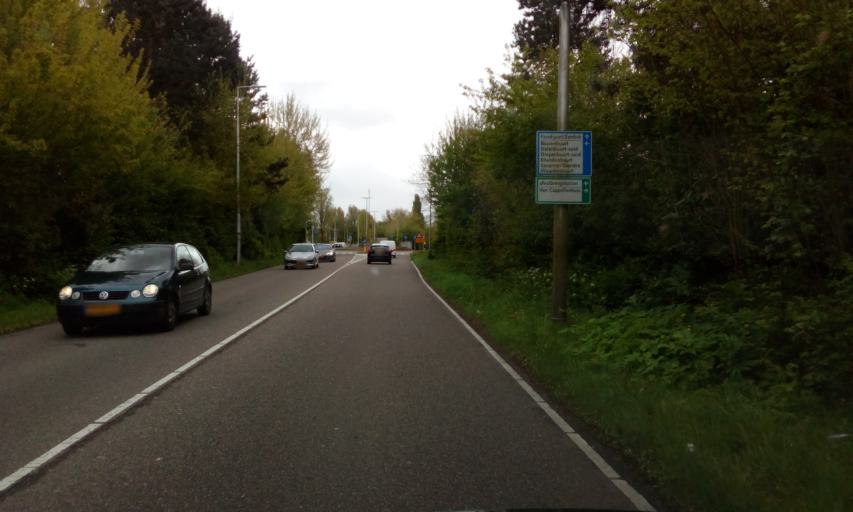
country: NL
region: South Holland
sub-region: Gemeente Krimpen aan den IJssel
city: Krimpen aan den IJssel
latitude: 51.9327
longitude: 4.5972
